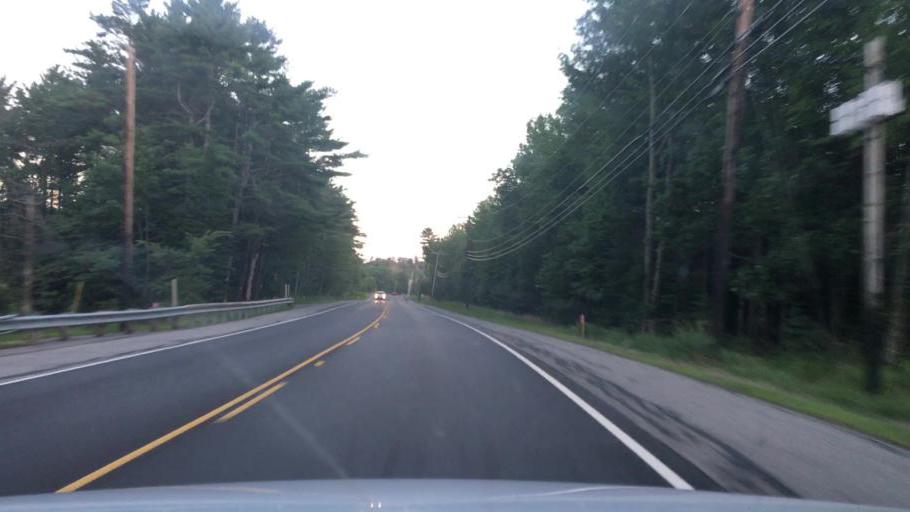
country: US
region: Maine
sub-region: Androscoggin County
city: Turner
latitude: 44.2296
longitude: -70.2537
